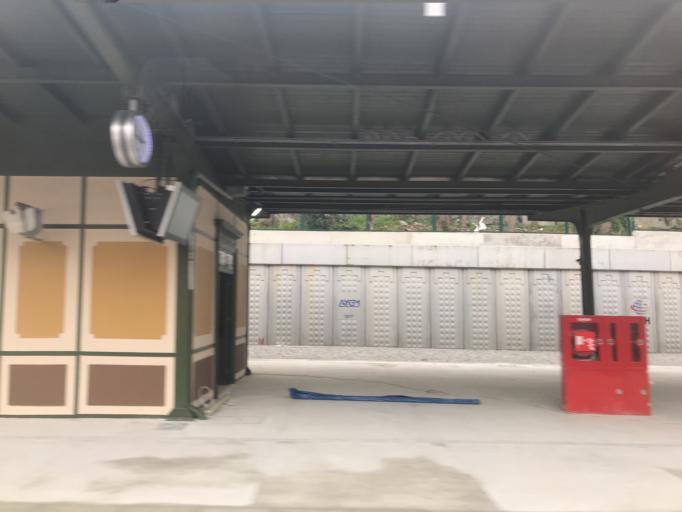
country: TR
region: Istanbul
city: Bahcelievler
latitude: 40.9802
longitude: 28.8721
